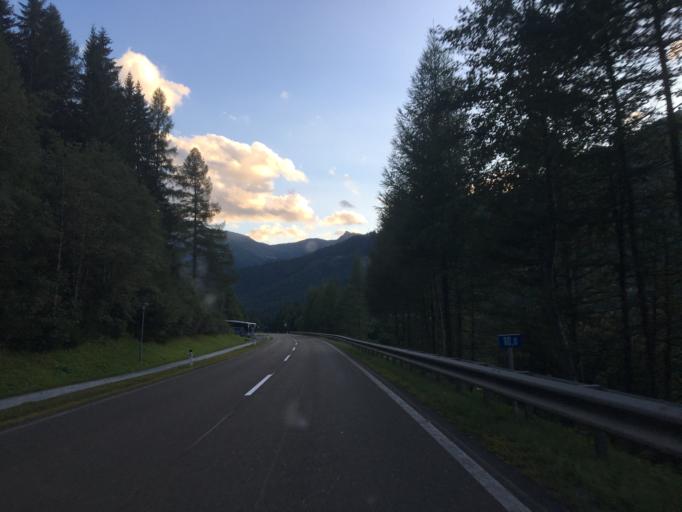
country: AT
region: Styria
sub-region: Politischer Bezirk Murtal
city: Hohentauern
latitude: 47.4318
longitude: 14.4694
